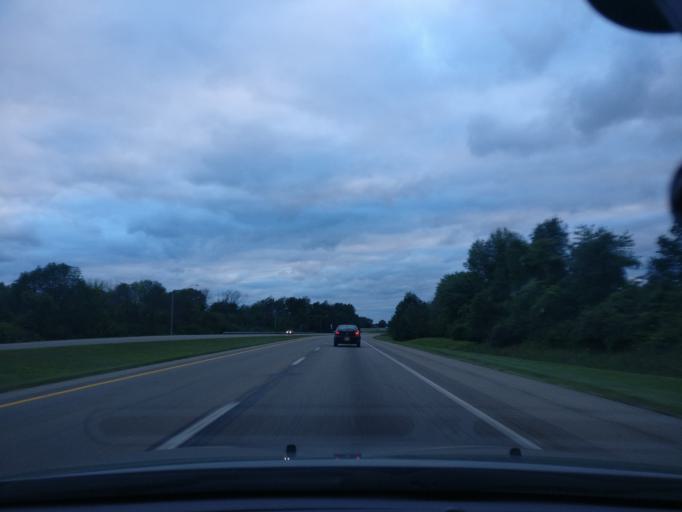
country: US
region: Ohio
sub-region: Greene County
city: Xenia
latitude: 39.6619
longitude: -83.9400
